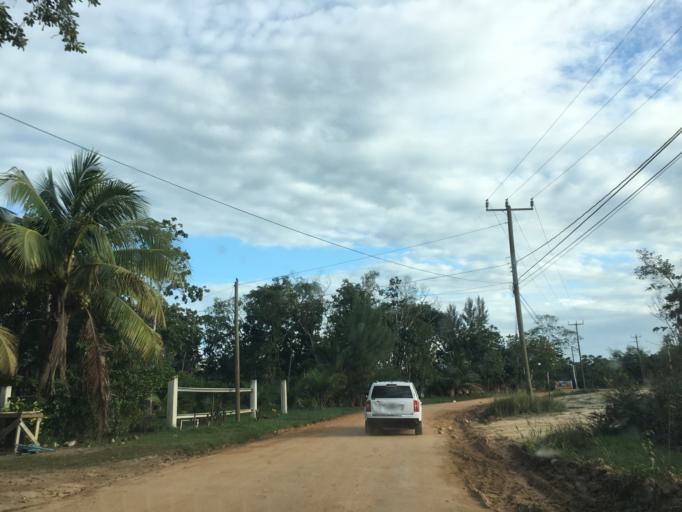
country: BZ
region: Stann Creek
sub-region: Dangriga
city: Dangriga
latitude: 16.8352
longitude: -88.2662
